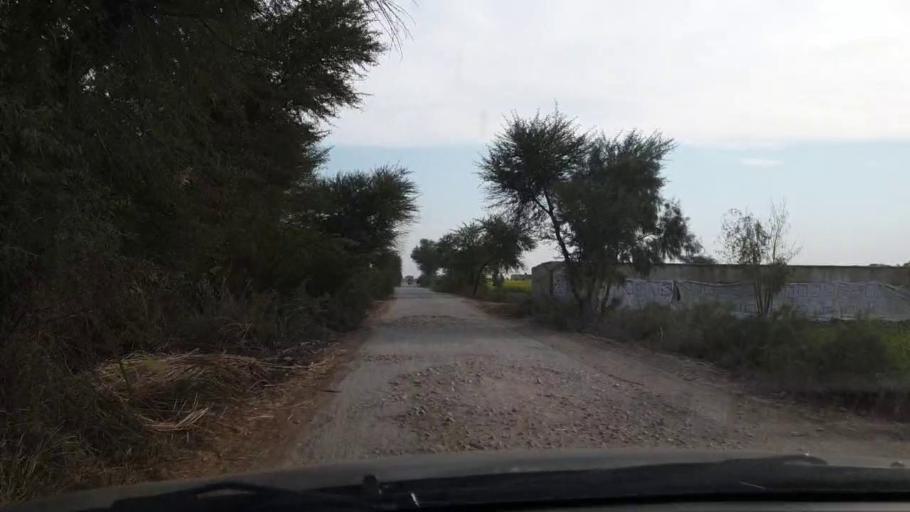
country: PK
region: Sindh
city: Khadro
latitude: 26.1211
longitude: 68.7960
